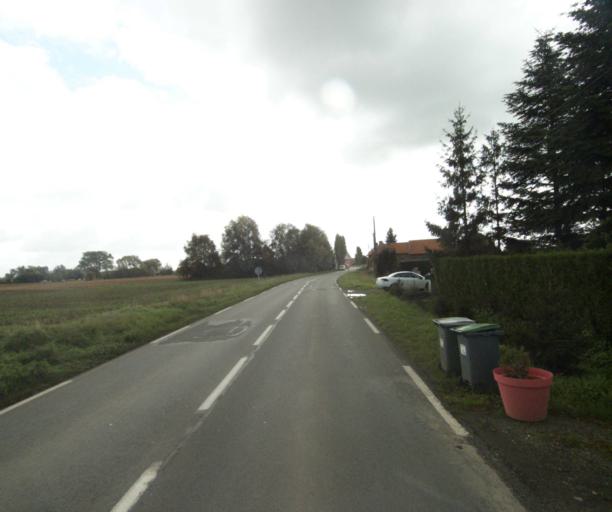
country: FR
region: Nord-Pas-de-Calais
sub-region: Departement du Nord
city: Perenchies
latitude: 50.6992
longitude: 2.9722
